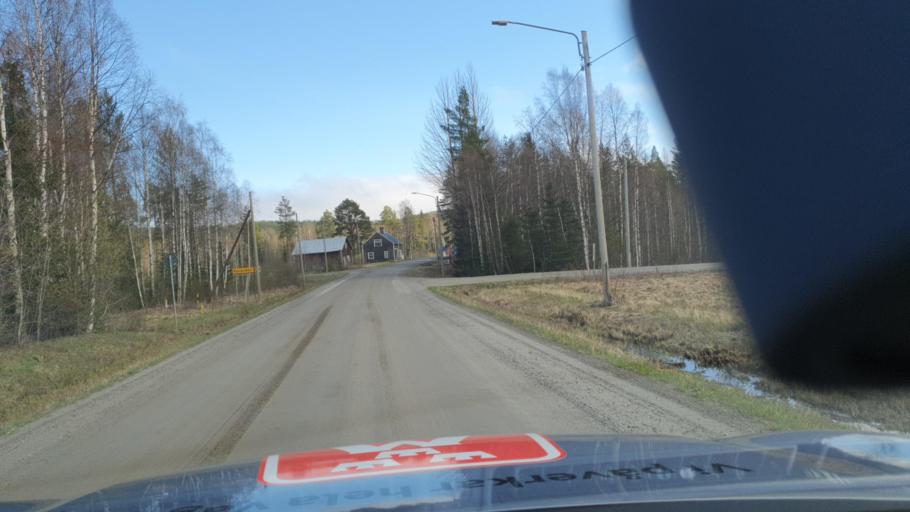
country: SE
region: Vaesterbotten
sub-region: Bjurholms Kommun
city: Bjurholm
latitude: 63.6990
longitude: 18.9439
